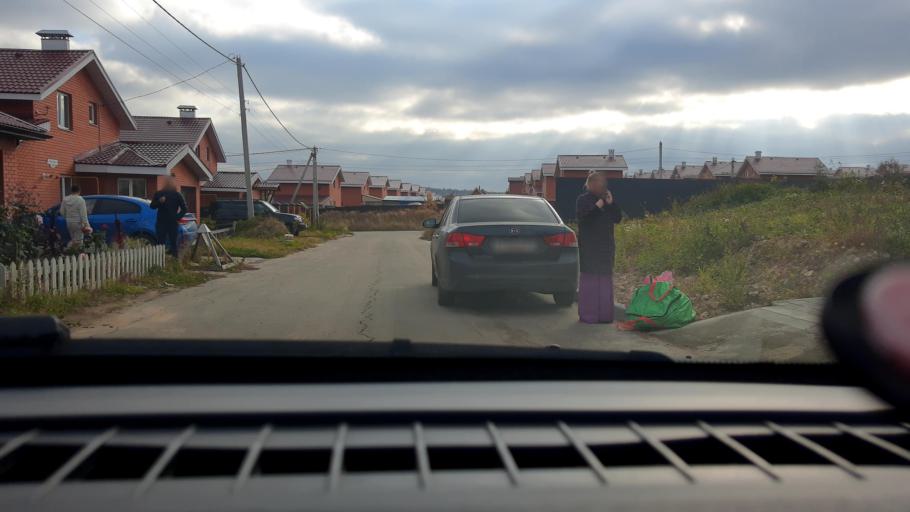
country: RU
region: Nizjnij Novgorod
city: Afonino
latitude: 56.1978
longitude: 44.0882
